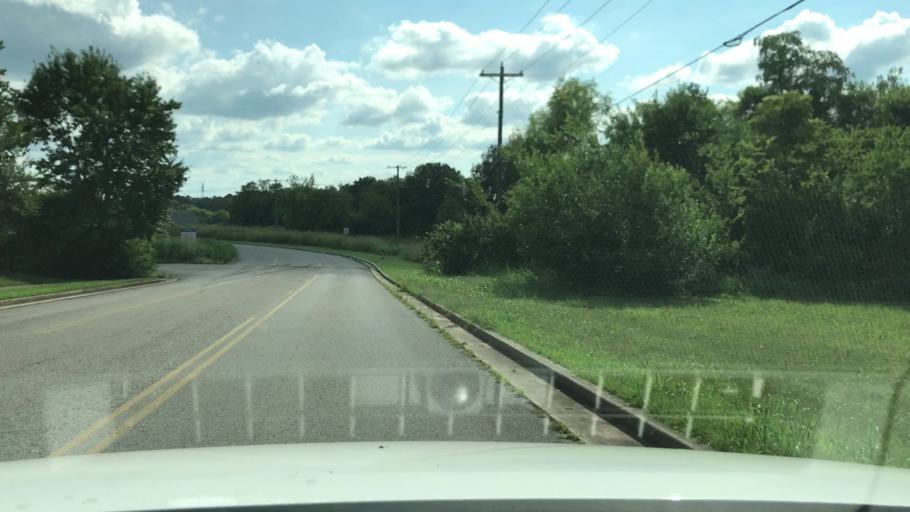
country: US
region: Tennessee
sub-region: Sumner County
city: Gallatin
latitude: 36.3771
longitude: -86.4801
